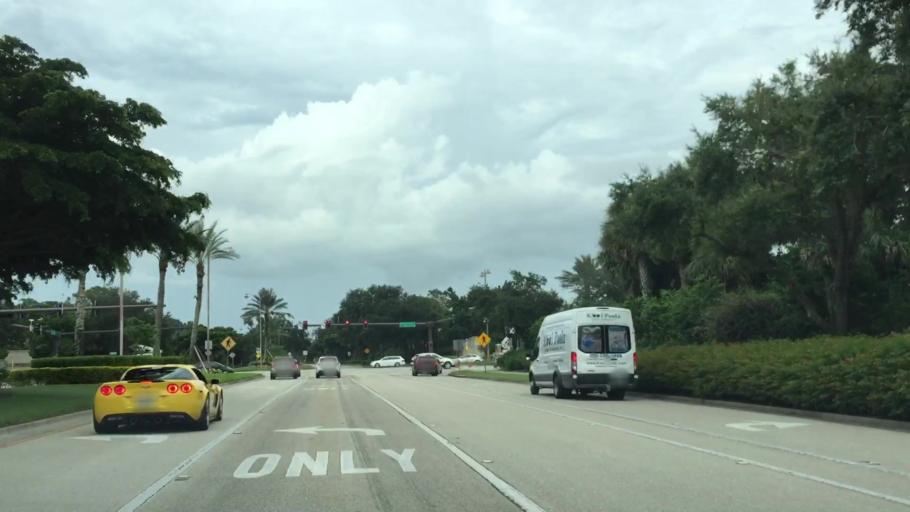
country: US
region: Florida
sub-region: Lee County
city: Estero
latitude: 26.3960
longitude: -81.7855
